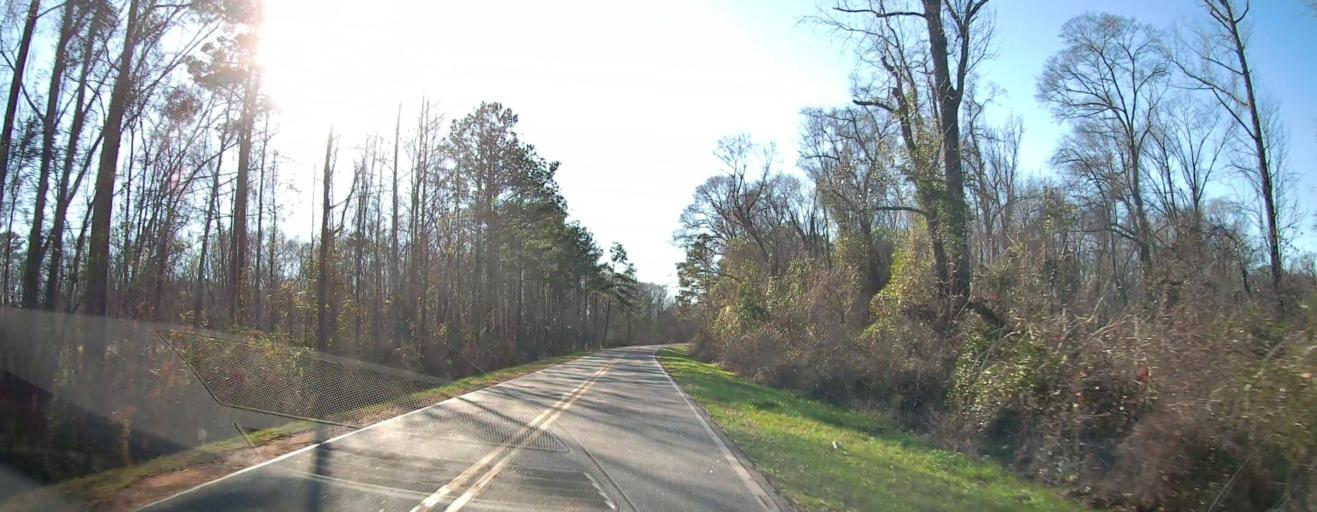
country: US
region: Georgia
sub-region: Sumter County
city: Americus
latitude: 32.0067
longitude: -84.2222
